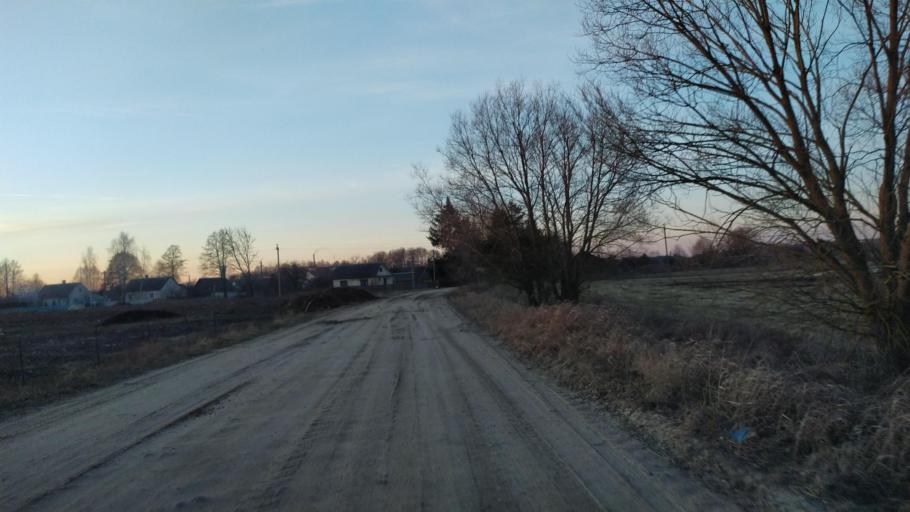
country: BY
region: Brest
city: Pruzhany
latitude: 52.5515
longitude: 24.2308
